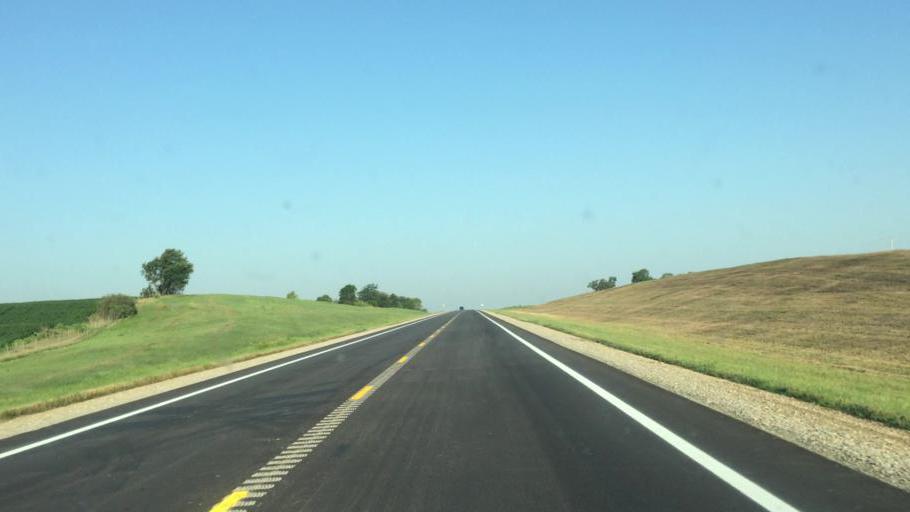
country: US
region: Kansas
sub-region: Doniphan County
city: Highland
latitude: 39.8412
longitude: -95.3832
